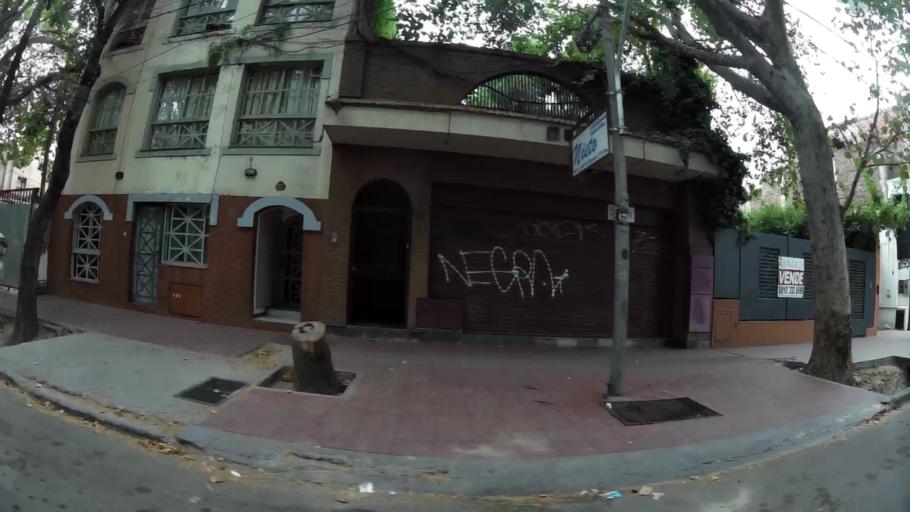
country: AR
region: Mendoza
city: Mendoza
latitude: -32.8824
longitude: -68.8399
